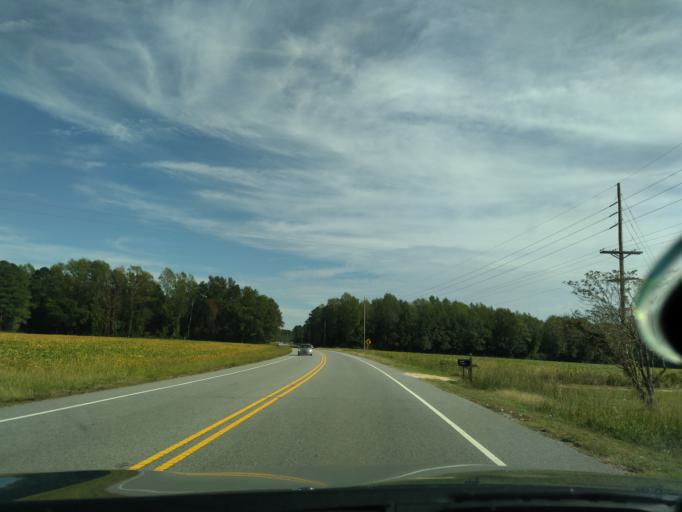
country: US
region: North Carolina
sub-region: Beaufort County
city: River Road
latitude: 35.5247
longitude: -76.9406
